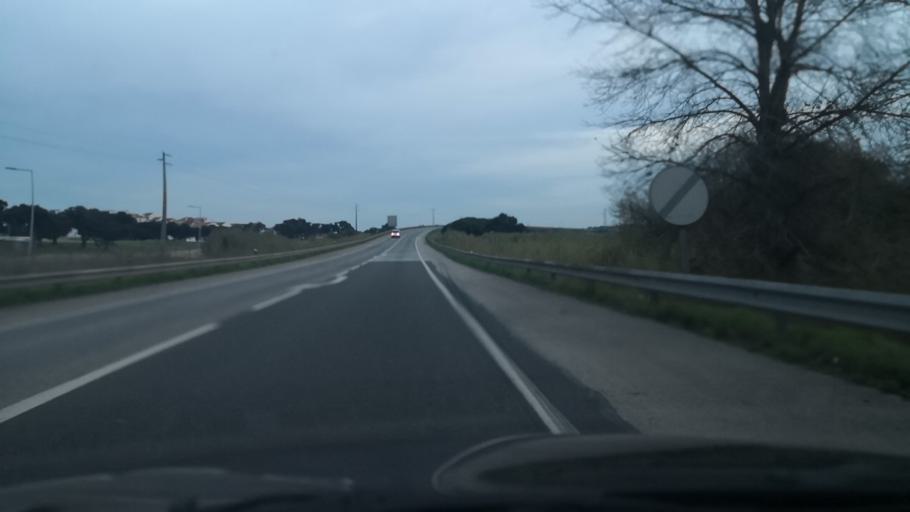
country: PT
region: Setubal
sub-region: Setubal
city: Setubal
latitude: 38.5208
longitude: -8.8414
